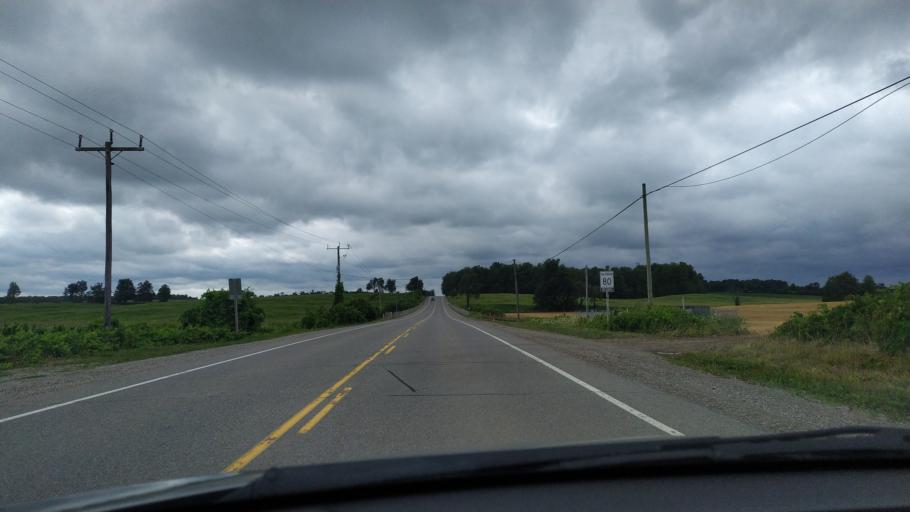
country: CA
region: Ontario
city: Kitchener
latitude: 43.3571
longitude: -80.4868
